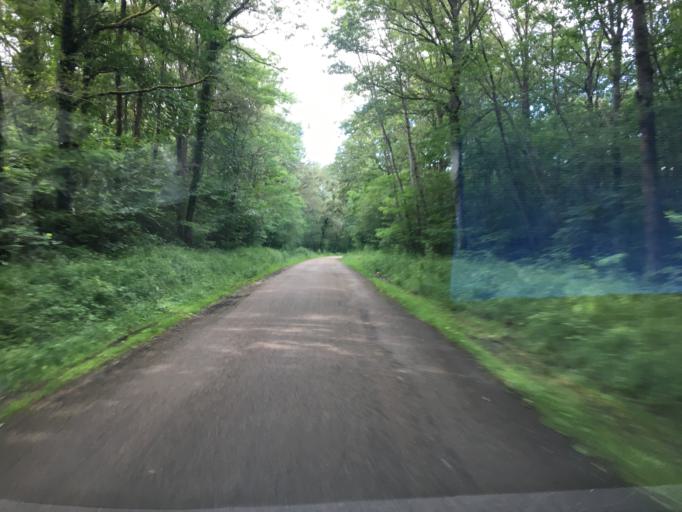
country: FR
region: Bourgogne
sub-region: Departement de l'Yonne
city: Charbuy
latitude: 47.8524
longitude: 3.4878
